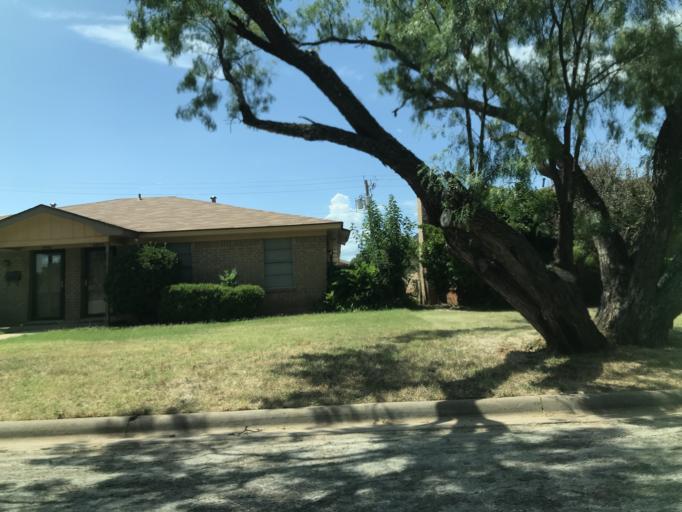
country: US
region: Texas
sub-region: Taylor County
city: Abilene
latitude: 32.4451
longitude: -99.7852
